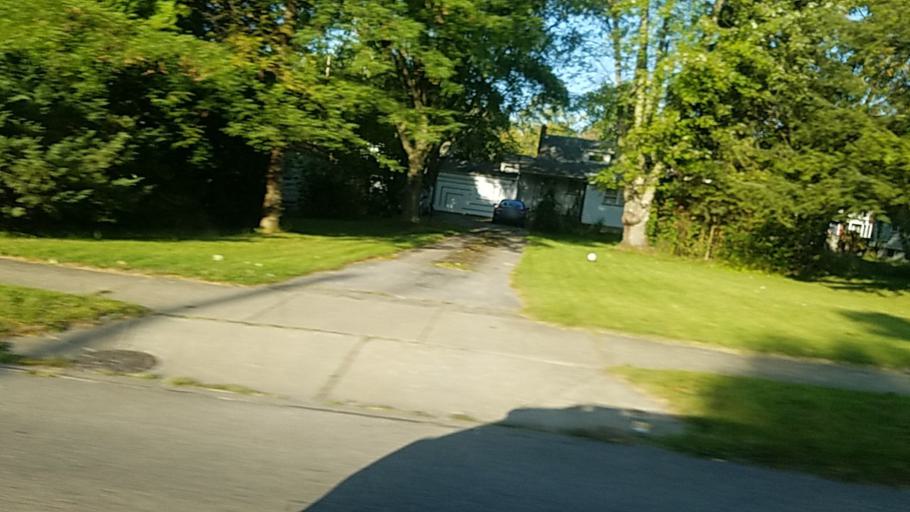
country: US
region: Ohio
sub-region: Mahoning County
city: Boardman
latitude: 41.0564
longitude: -80.6579
